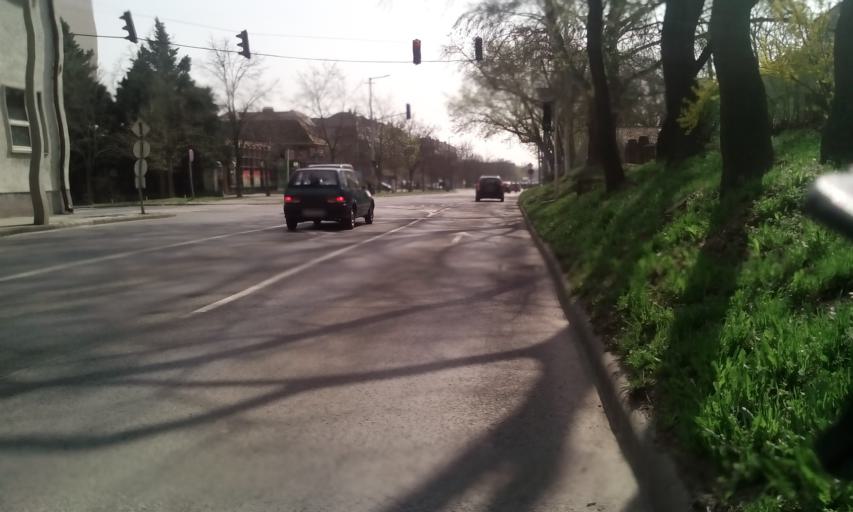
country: HU
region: Tolna
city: Szekszard
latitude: 46.3451
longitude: 18.7011
